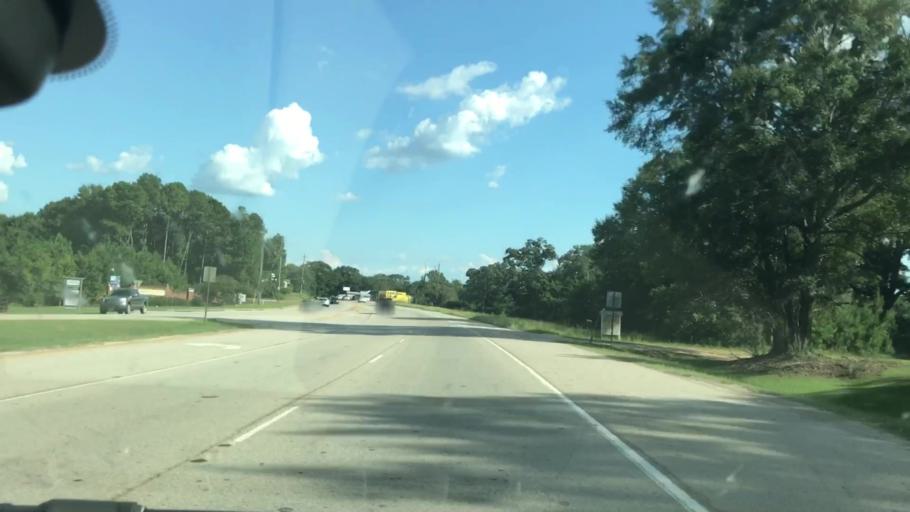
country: US
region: Georgia
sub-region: Troup County
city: La Grange
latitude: 32.9964
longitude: -85.0096
